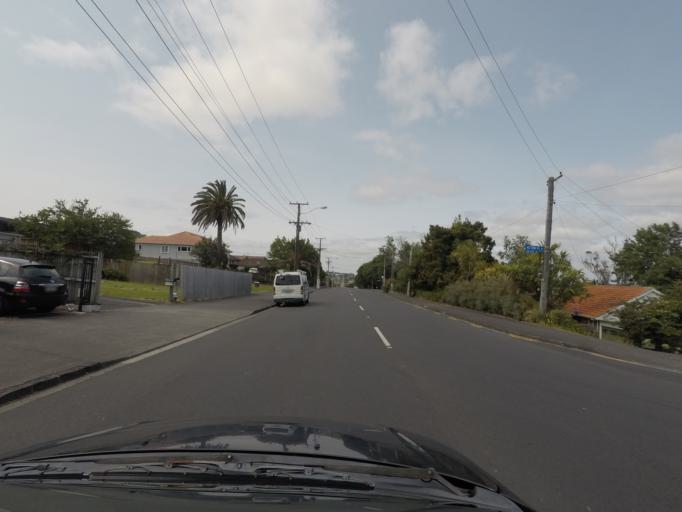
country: NZ
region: Auckland
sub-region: Auckland
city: Rosebank
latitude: -36.9019
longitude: 174.7014
